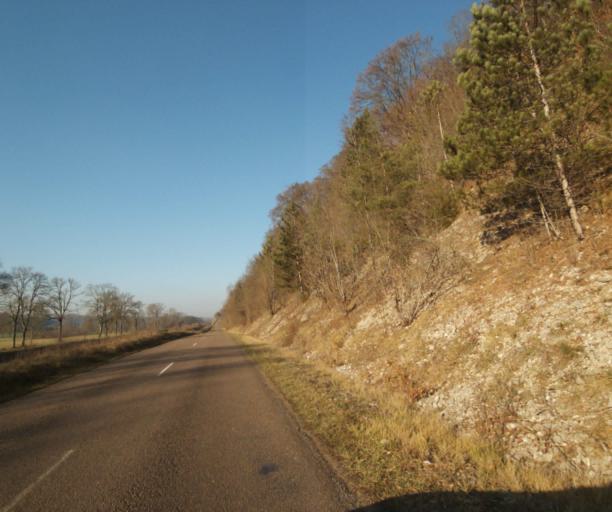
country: FR
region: Champagne-Ardenne
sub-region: Departement de la Haute-Marne
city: Chevillon
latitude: 48.5091
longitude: 5.1228
